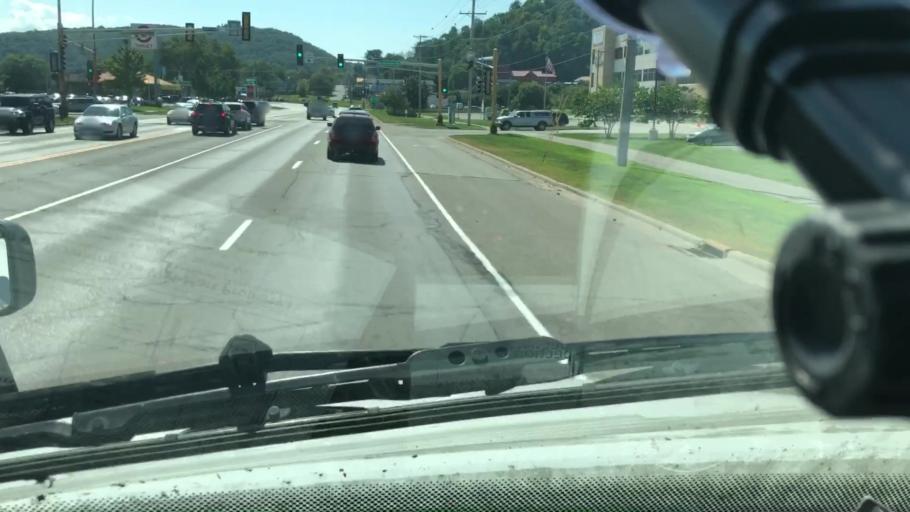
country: US
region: Minnesota
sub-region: Winona County
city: Winona
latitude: 44.0336
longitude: -91.6222
